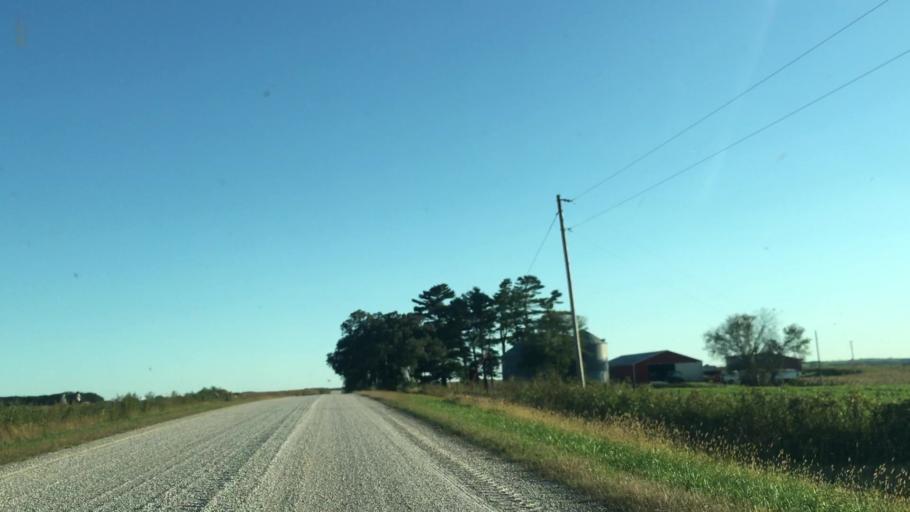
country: US
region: Minnesota
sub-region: Fillmore County
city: Preston
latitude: 43.8096
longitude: -92.0396
